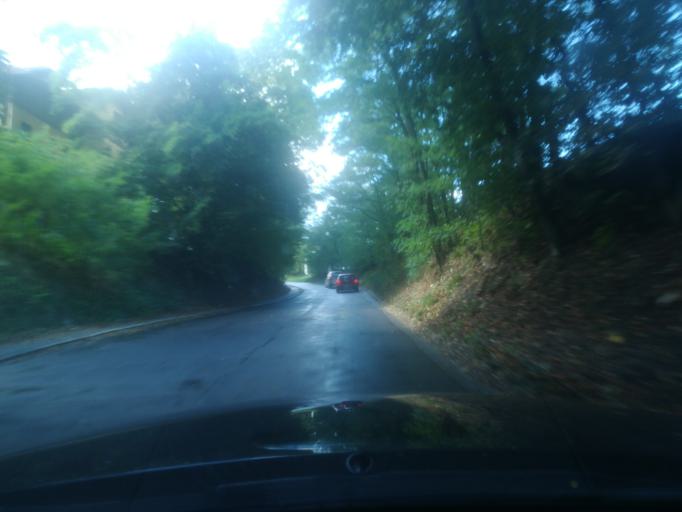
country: AT
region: Upper Austria
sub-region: Linz Stadt
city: Linz
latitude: 48.3352
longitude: 14.2799
